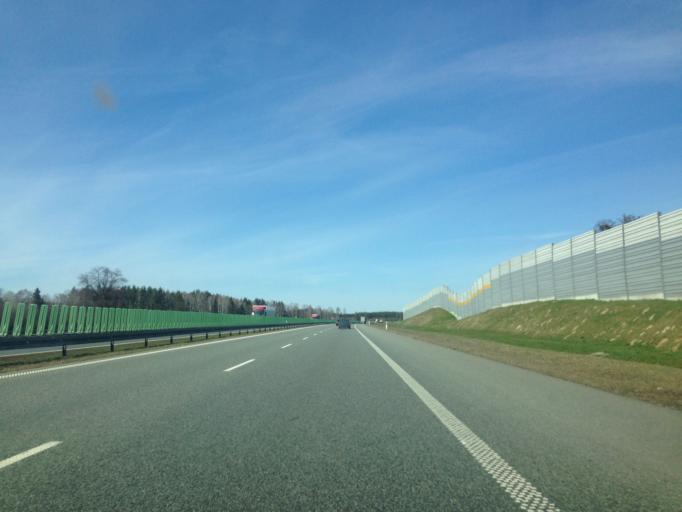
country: PL
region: Pomeranian Voivodeship
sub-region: Powiat starogardzki
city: Bobowo
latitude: 53.8726
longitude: 18.6284
